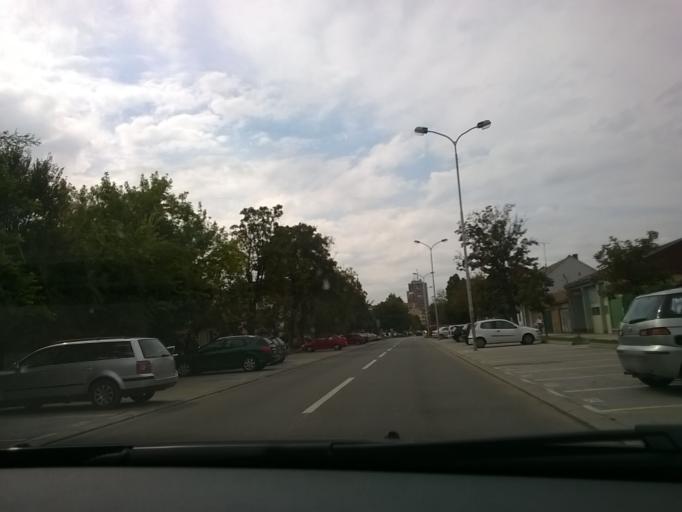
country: RS
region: Autonomna Pokrajina Vojvodina
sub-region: Juznobanatski Okrug
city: Pancevo
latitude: 44.8760
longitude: 20.6487
